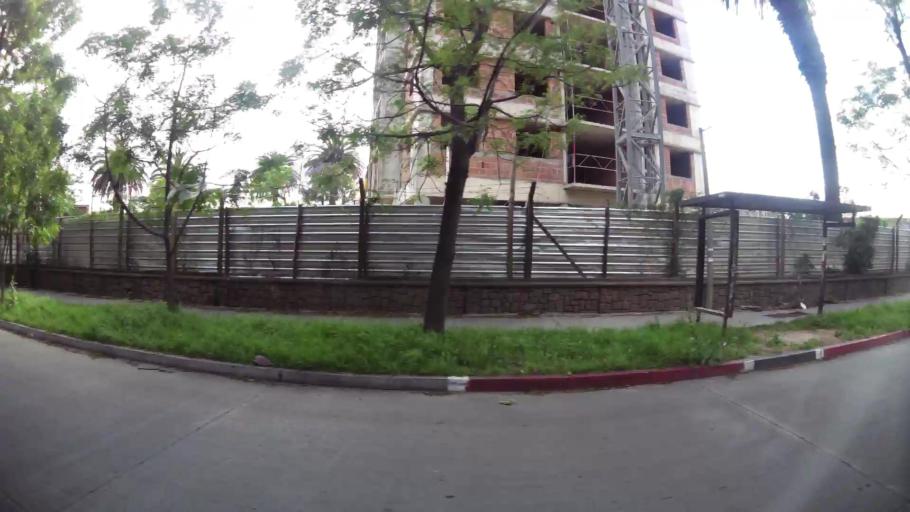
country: UY
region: Montevideo
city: Montevideo
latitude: -34.8808
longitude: -56.1651
